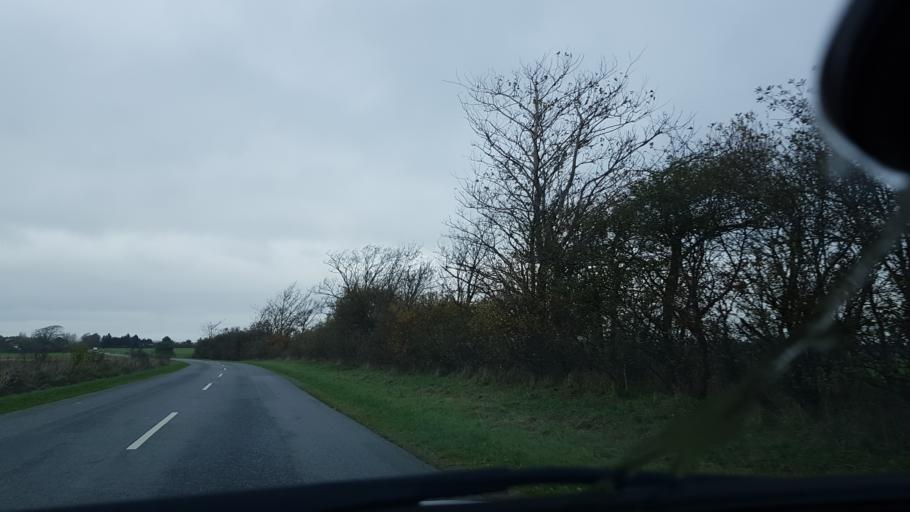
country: DK
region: South Denmark
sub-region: Tonder Kommune
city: Sherrebek
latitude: 55.2251
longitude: 8.8345
